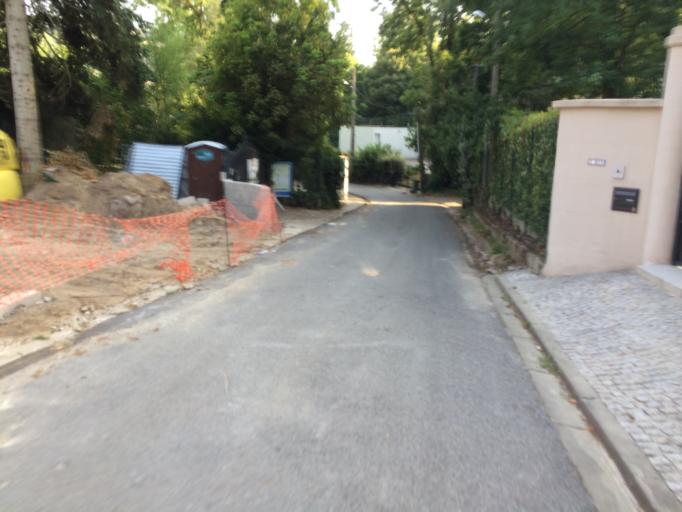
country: FR
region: Ile-de-France
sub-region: Departement de l'Essonne
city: Igny
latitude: 48.7494
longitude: 2.2328
